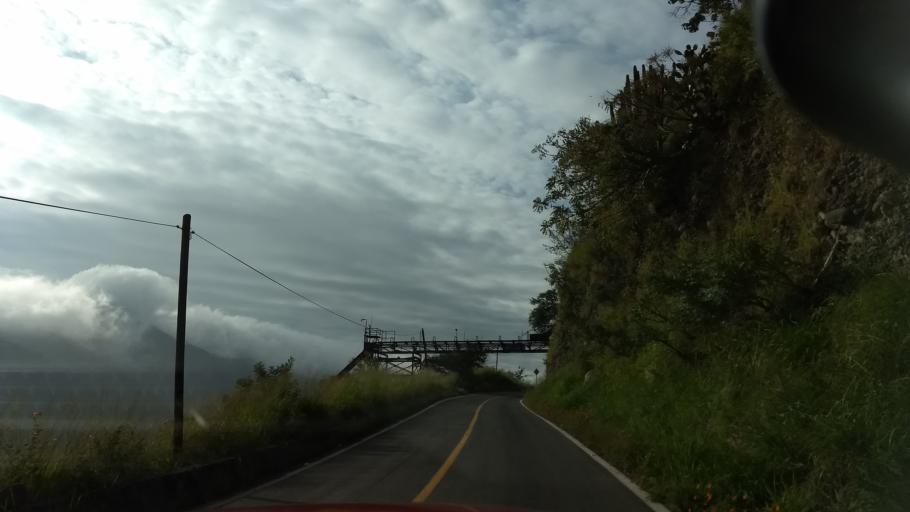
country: MX
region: Jalisco
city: Tuxpan
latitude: 19.5247
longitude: -103.4405
